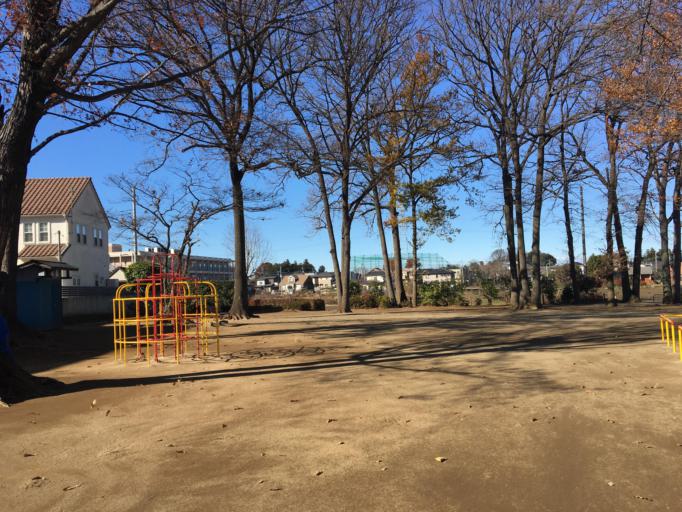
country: JP
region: Saitama
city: Sakado
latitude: 35.9380
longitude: 139.4162
